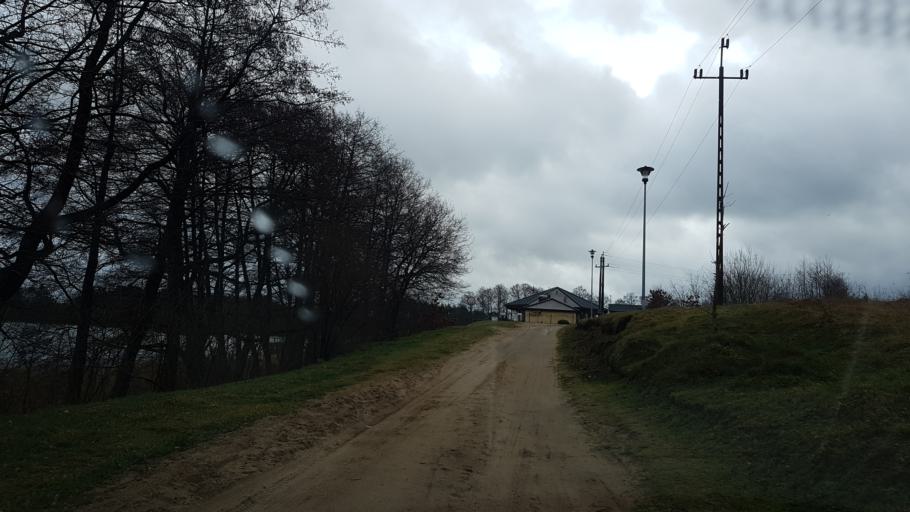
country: PL
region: West Pomeranian Voivodeship
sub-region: Powiat drawski
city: Czaplinek
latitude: 53.5506
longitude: 16.2485
